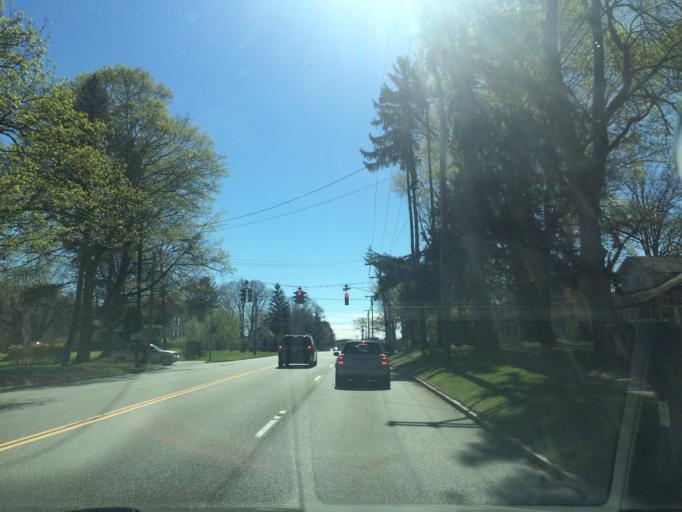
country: US
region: New York
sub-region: Monroe County
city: East Rochester
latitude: 43.1051
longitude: -77.4898
